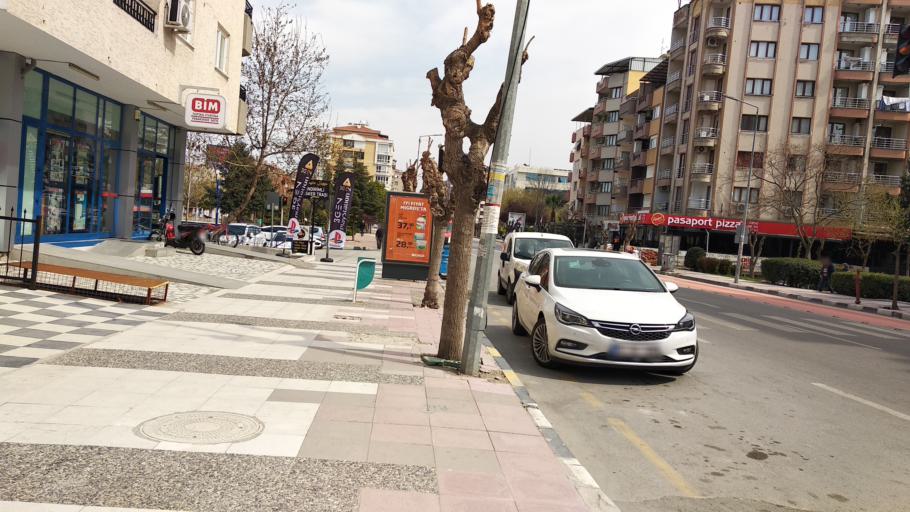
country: TR
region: Manisa
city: Manisa
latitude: 38.6126
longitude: 27.4123
